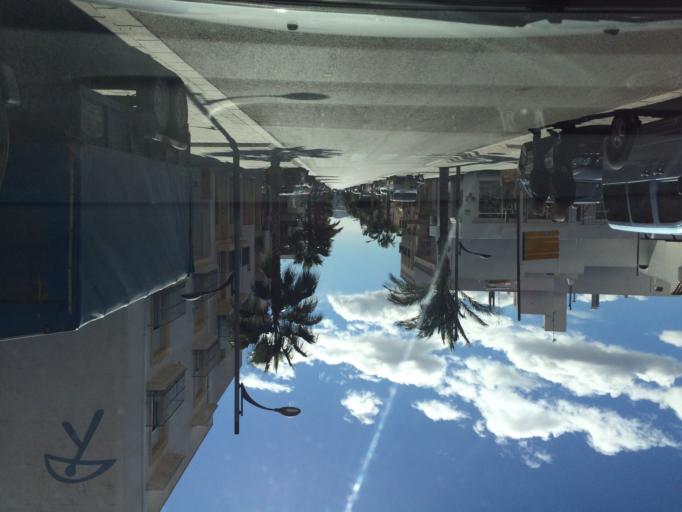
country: ES
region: Andalusia
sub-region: Provincia de Almeria
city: Nijar
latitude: 36.9622
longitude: -2.2066
